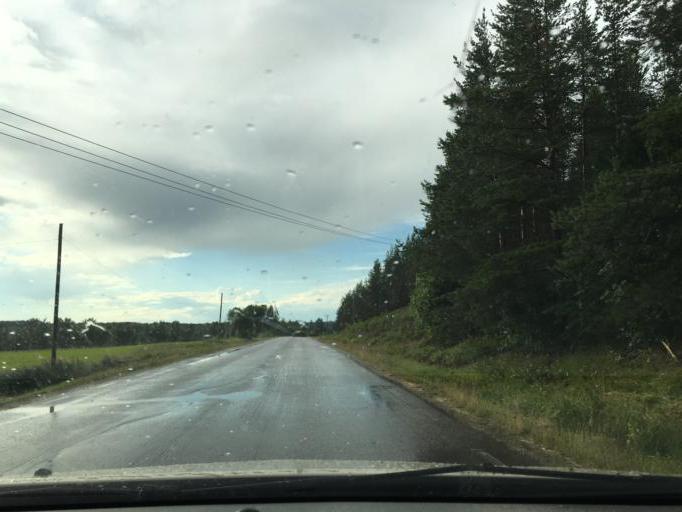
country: SE
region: Norrbotten
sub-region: Kalix Kommun
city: Toere
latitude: 65.9523
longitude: 22.8889
